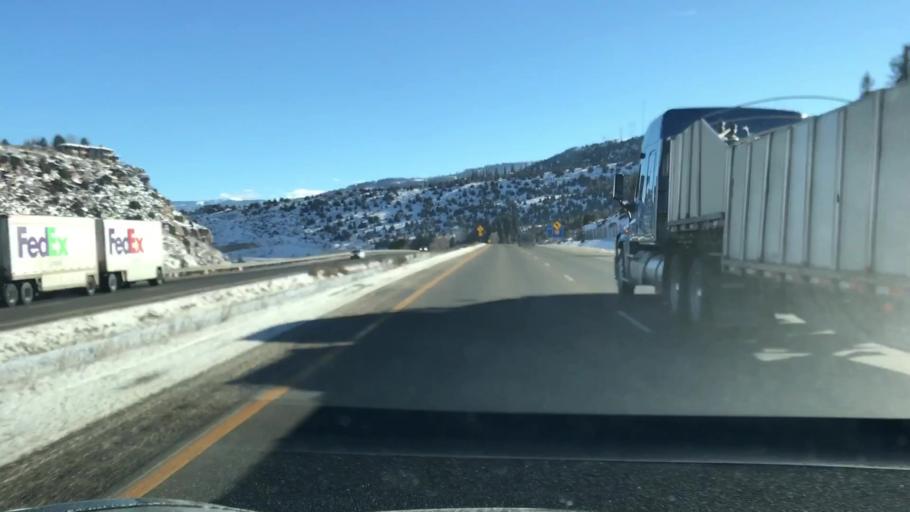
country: US
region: Colorado
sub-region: Eagle County
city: Edwards
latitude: 39.7069
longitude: -106.6916
